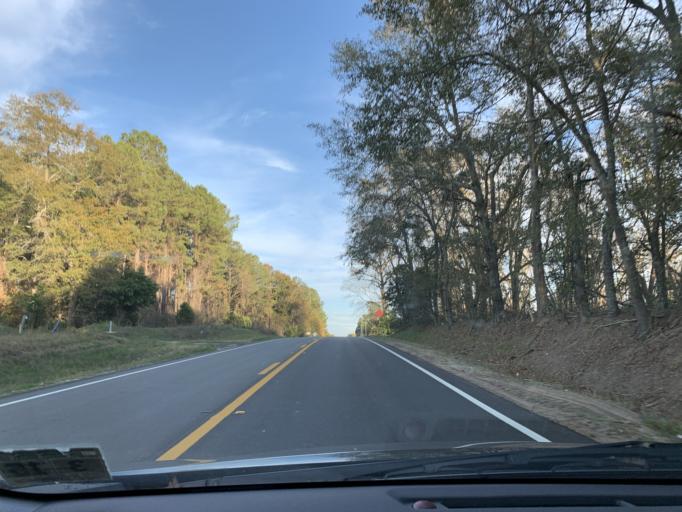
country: US
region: Georgia
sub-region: Irwin County
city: Ocilla
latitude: 31.5957
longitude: -83.1401
